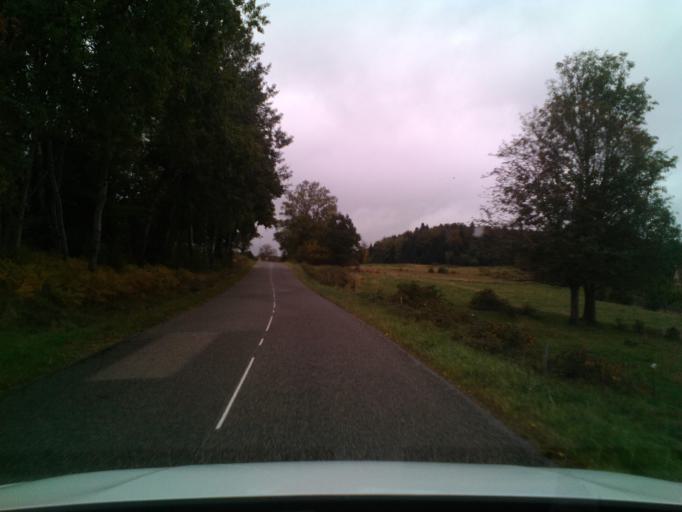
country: FR
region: Lorraine
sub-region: Departement des Vosges
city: Senones
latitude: 48.3633
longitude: 6.9697
